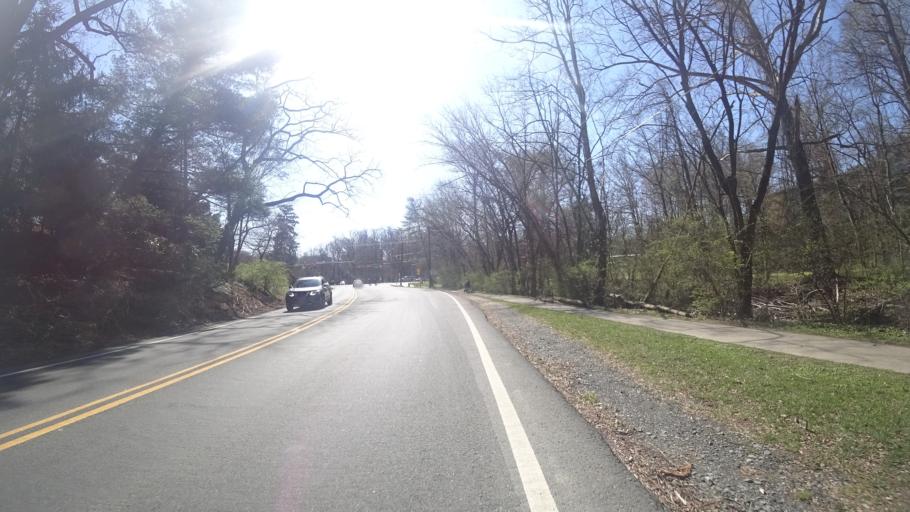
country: US
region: Maryland
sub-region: Montgomery County
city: Four Corners
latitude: 39.0084
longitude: -77.0211
